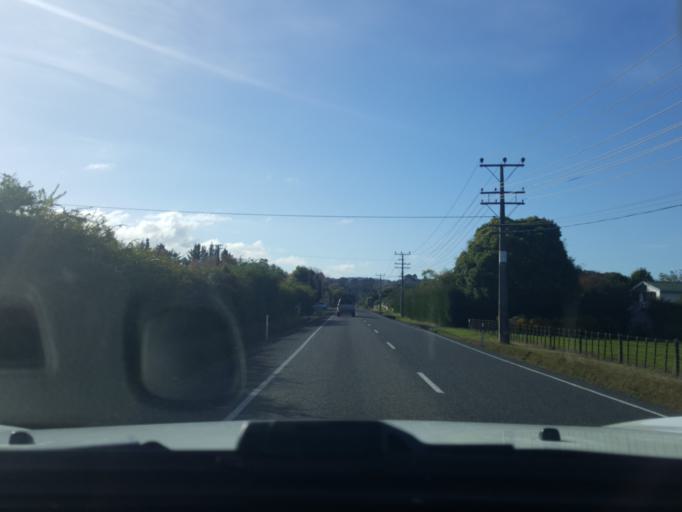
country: NZ
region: Auckland
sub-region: Auckland
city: Muriwai Beach
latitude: -36.7679
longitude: 174.5763
